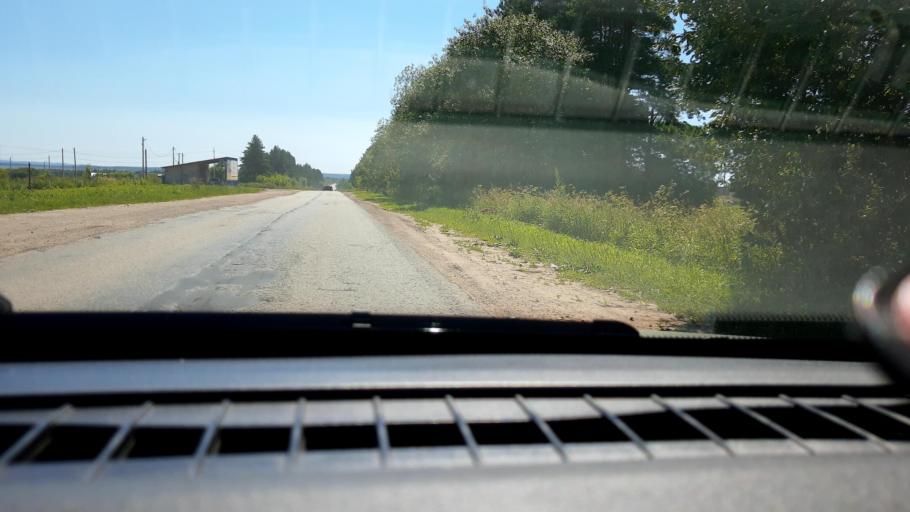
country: RU
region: Nizjnij Novgorod
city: Burevestnik
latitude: 56.1544
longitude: 43.7771
